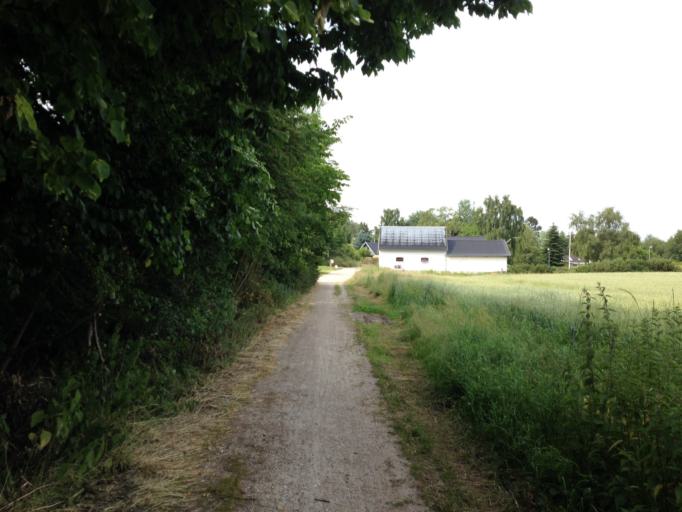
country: DK
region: Capital Region
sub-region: Fredensborg Kommune
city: Niva
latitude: 55.9506
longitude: 12.5072
